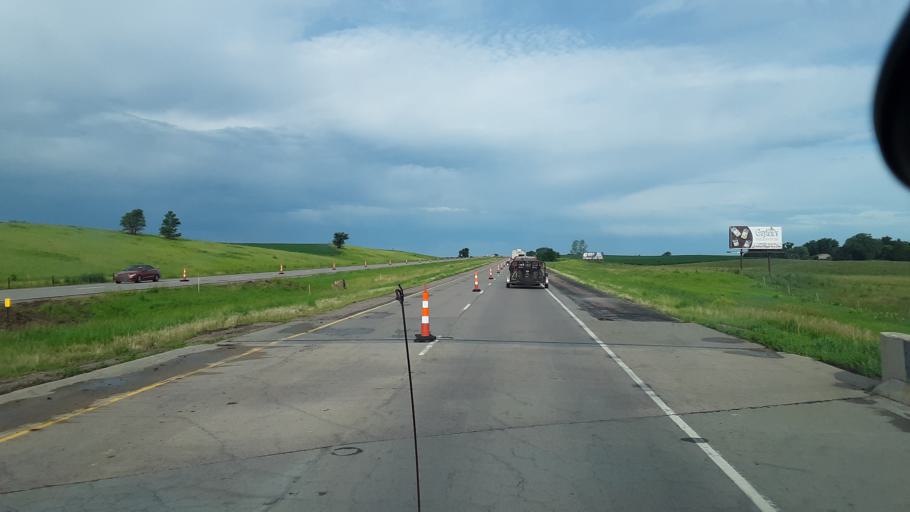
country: US
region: South Dakota
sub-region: Minnehaha County
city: Crooks
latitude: 43.6087
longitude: -96.8422
